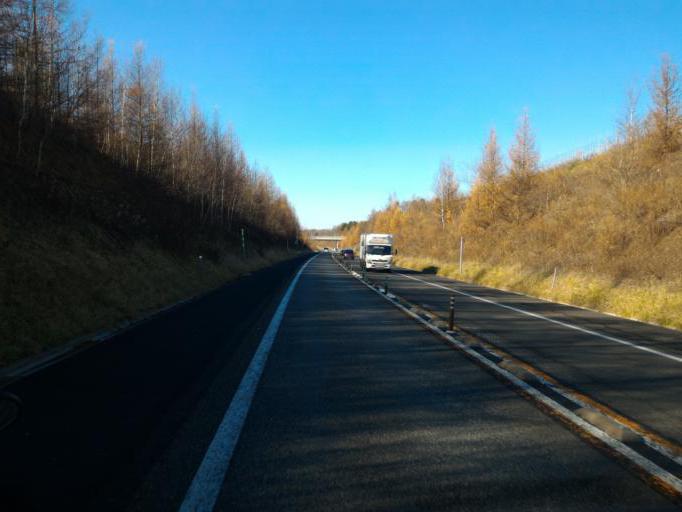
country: JP
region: Hokkaido
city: Chitose
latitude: 42.8966
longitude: 141.8582
